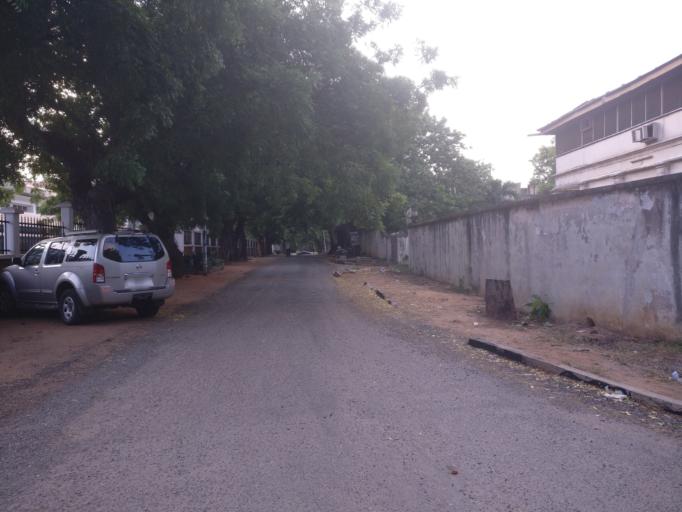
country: GH
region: Greater Accra
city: Accra
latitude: 5.5555
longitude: -0.1961
